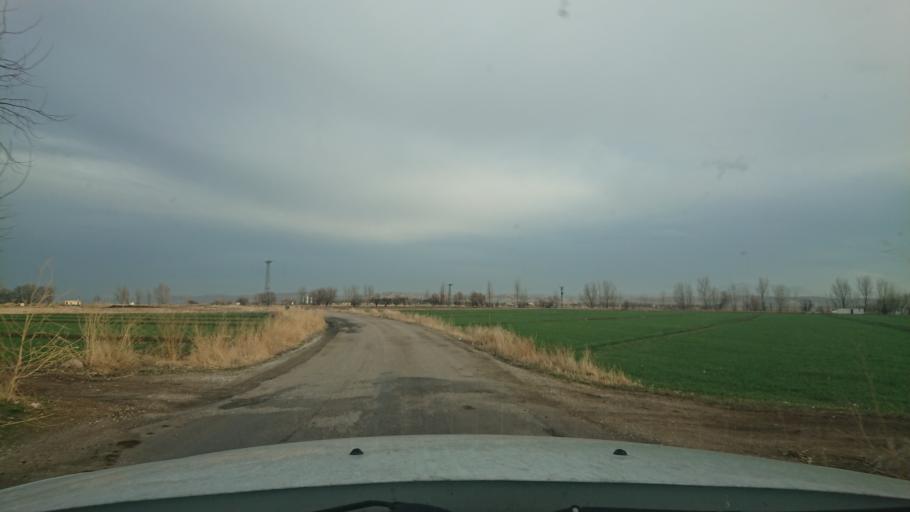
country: TR
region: Aksaray
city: Yesilova
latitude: 38.4425
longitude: 33.8369
